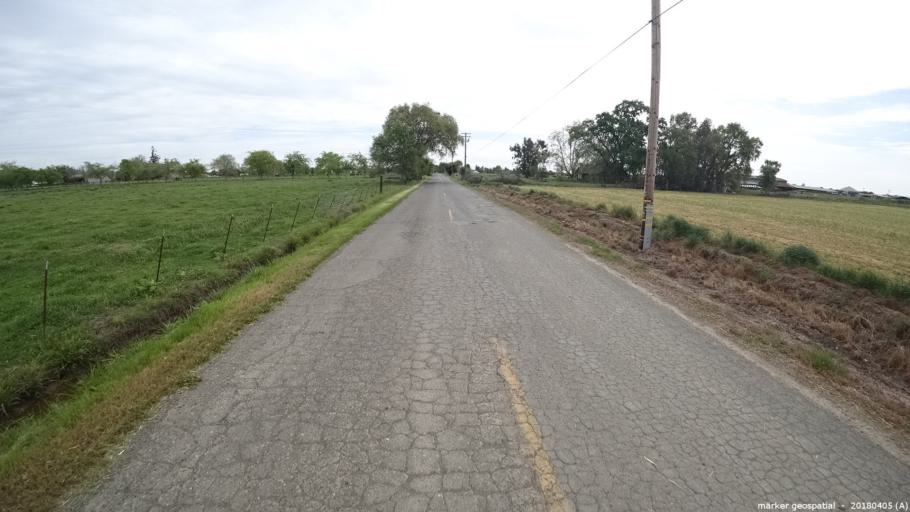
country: US
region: California
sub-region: Sacramento County
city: Galt
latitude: 38.2545
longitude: -121.3482
